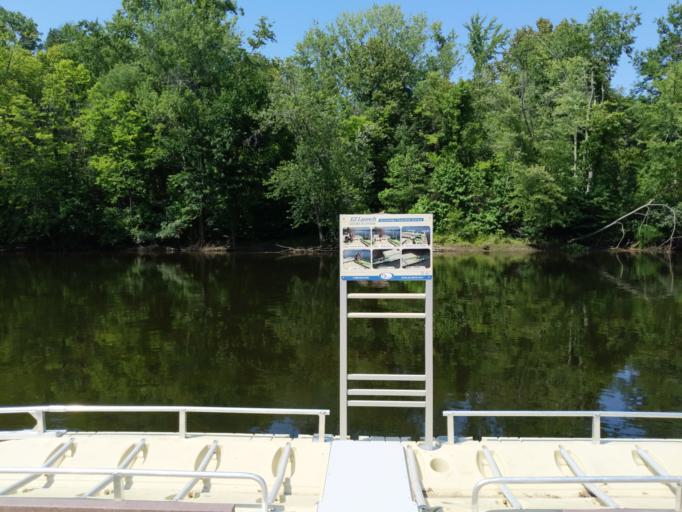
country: US
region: Michigan
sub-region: Eaton County
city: Grand Ledge
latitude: 42.7571
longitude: -84.7099
